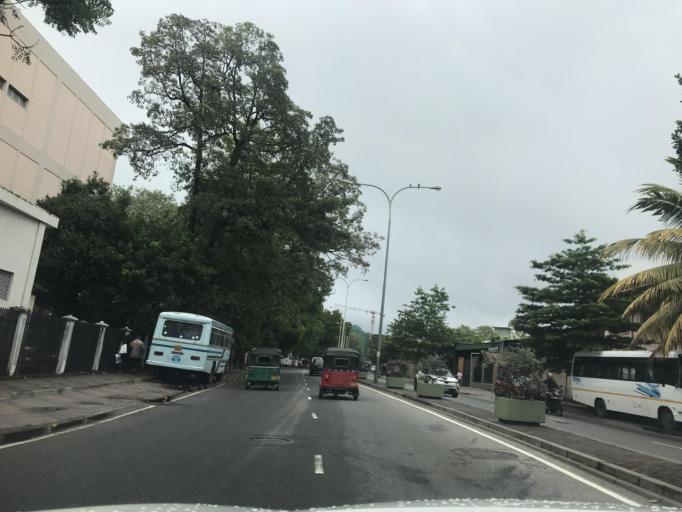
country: LK
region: Western
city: Colombo
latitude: 6.9212
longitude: 79.8643
